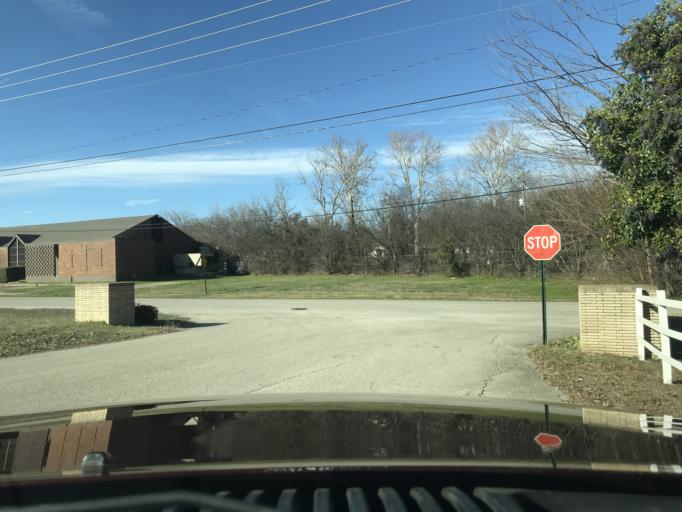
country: US
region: Texas
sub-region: Tarrant County
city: Edgecliff Village
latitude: 32.6613
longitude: -97.3431
